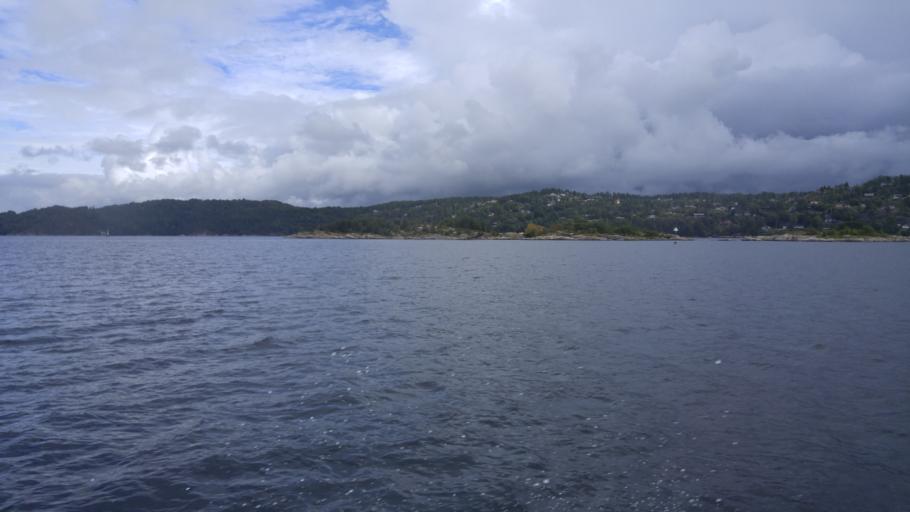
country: NO
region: Akershus
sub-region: Nesodden
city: Fagerstrand
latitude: 59.6984
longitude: 10.5841
